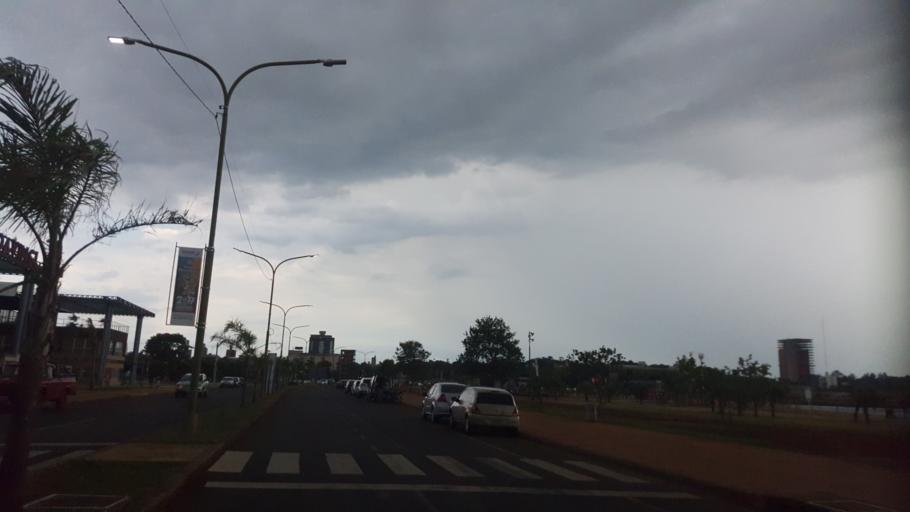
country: AR
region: Misiones
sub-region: Departamento de Capital
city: Posadas
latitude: -27.3536
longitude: -55.9023
